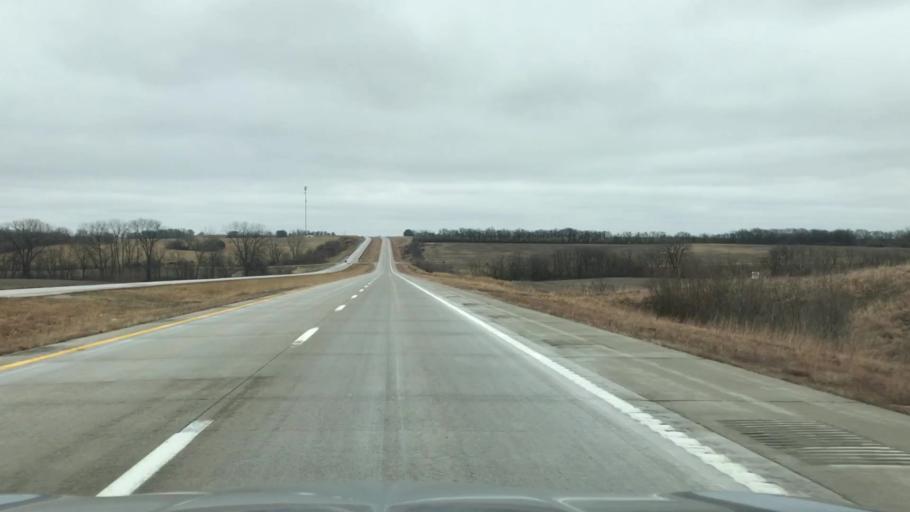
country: US
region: Missouri
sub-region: Caldwell County
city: Hamilton
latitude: 39.7346
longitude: -93.7839
